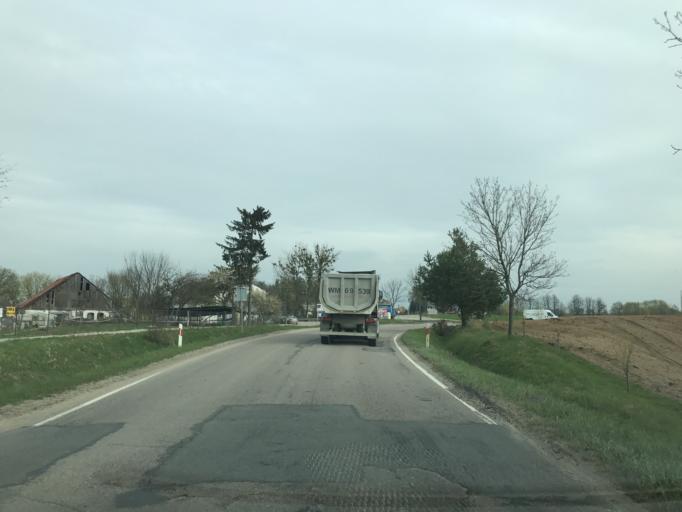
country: PL
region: Warmian-Masurian Voivodeship
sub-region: Powiat ostrodzki
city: Gierzwald
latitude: 53.5833
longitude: 20.0886
